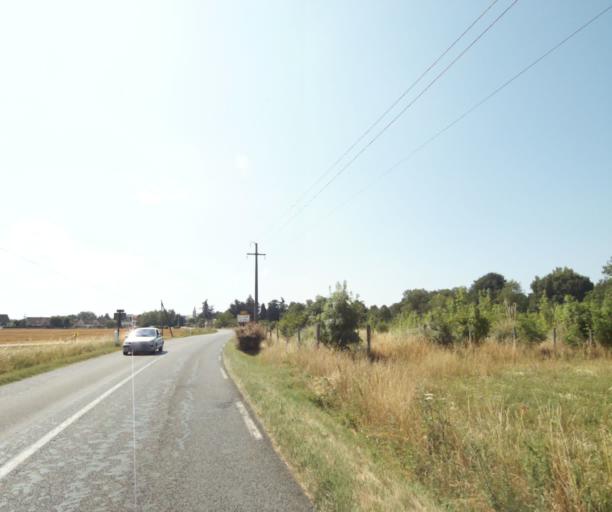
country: FR
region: Centre
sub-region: Departement du Loiret
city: Saint-Cyr-en-Val
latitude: 47.8375
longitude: 1.9650
